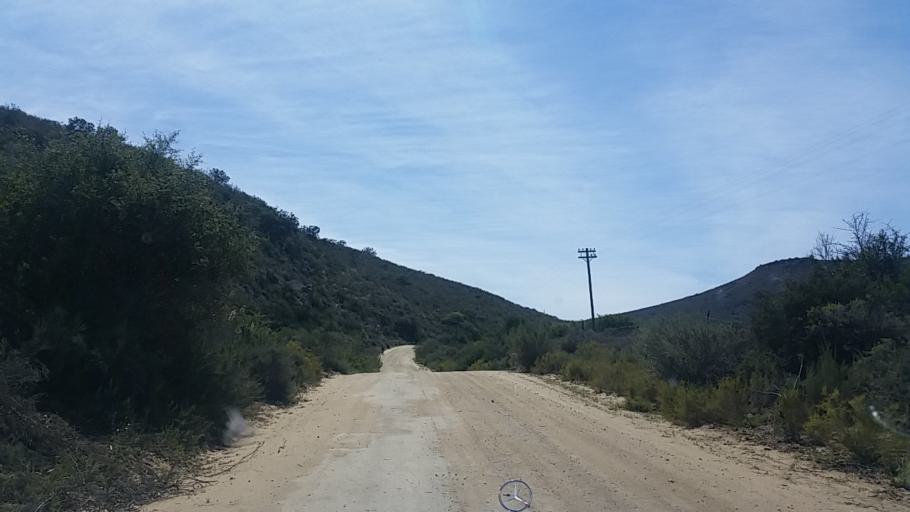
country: ZA
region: Western Cape
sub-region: Eden District Municipality
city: Knysna
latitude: -33.6400
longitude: 23.1449
